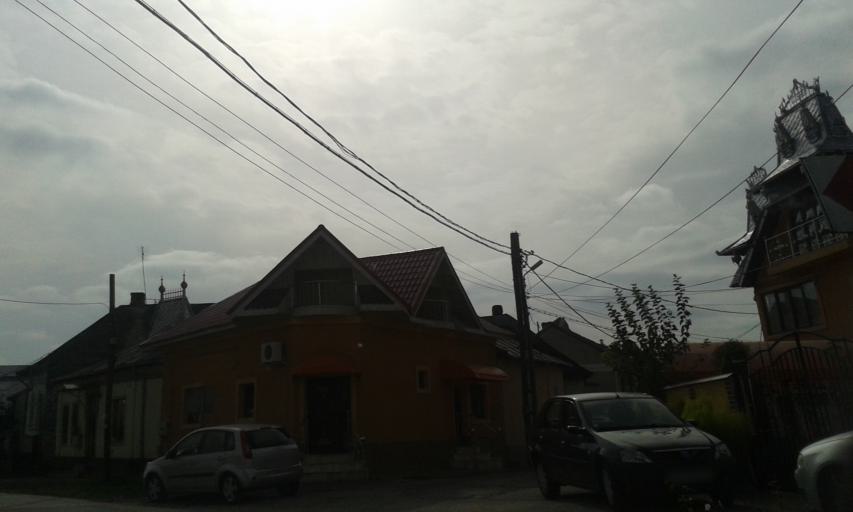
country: RO
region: Gorj
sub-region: Comuna Targu Carbunesti
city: Targu Carbunesti
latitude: 44.9524
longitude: 23.5135
